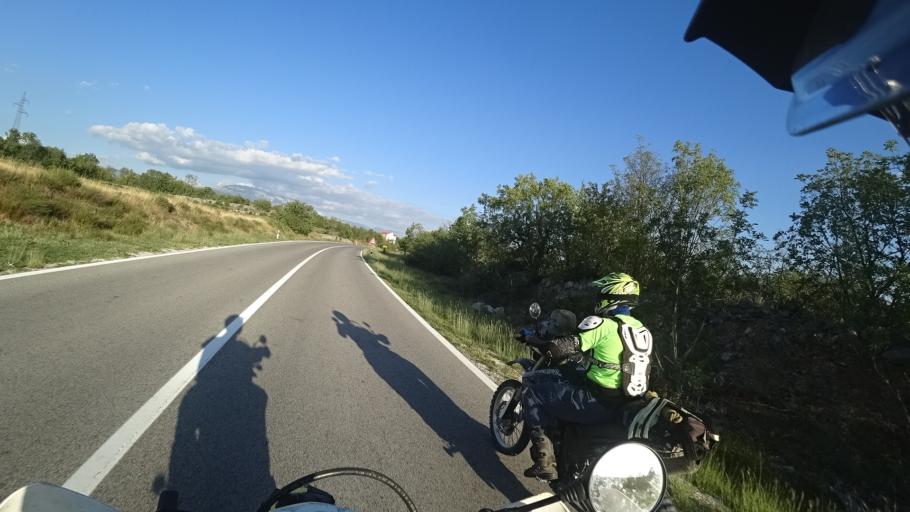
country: HR
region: Sibensko-Kniniska
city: Knin
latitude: 44.0593
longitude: 16.1797
